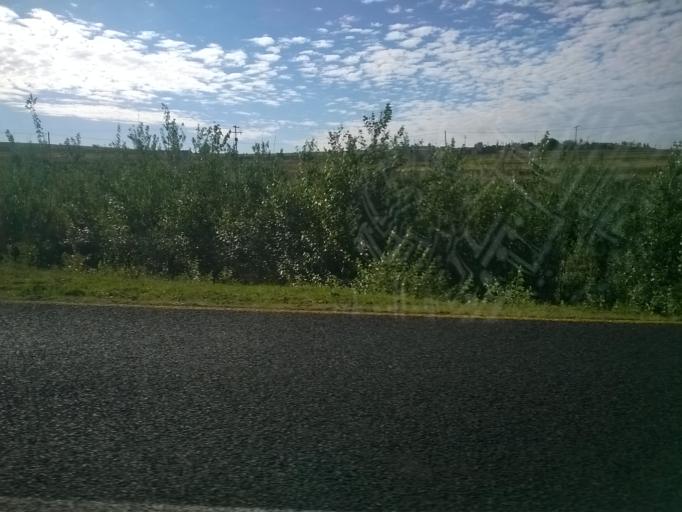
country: LS
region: Berea
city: Teyateyaneng
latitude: -29.1221
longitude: 27.7897
